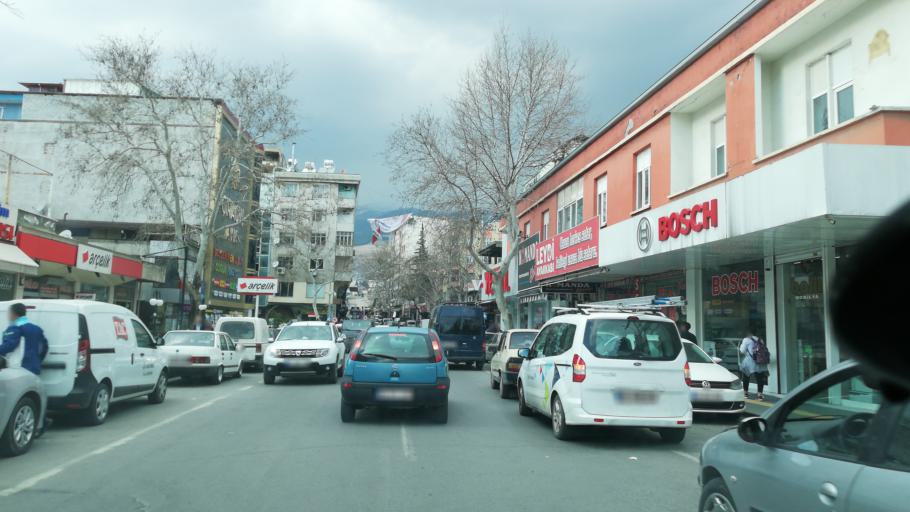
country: TR
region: Kahramanmaras
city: Kahramanmaras
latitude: 37.5807
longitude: 36.9304
